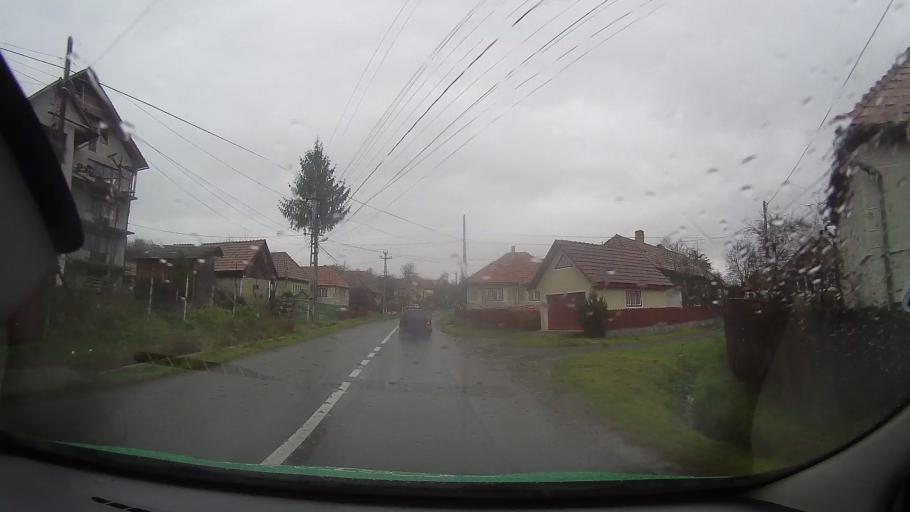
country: RO
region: Mures
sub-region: Comuna Brancovenesti
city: Valenii de Mures
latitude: 46.8942
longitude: 24.7967
